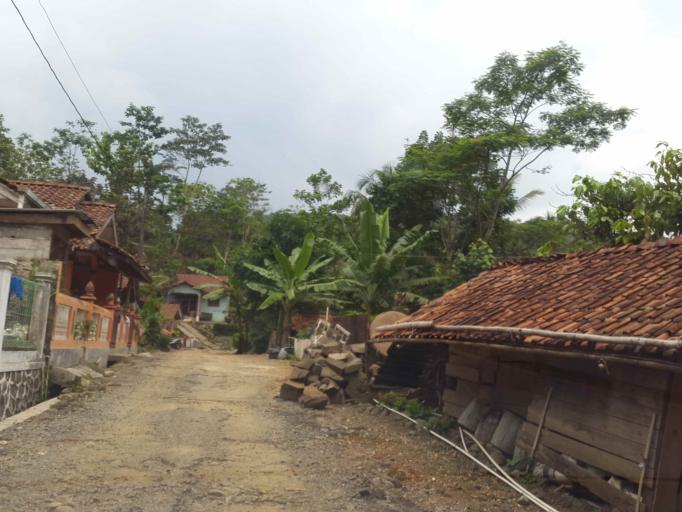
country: ID
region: Central Java
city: Bantarmangu
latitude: -7.3456
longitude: 108.9605
